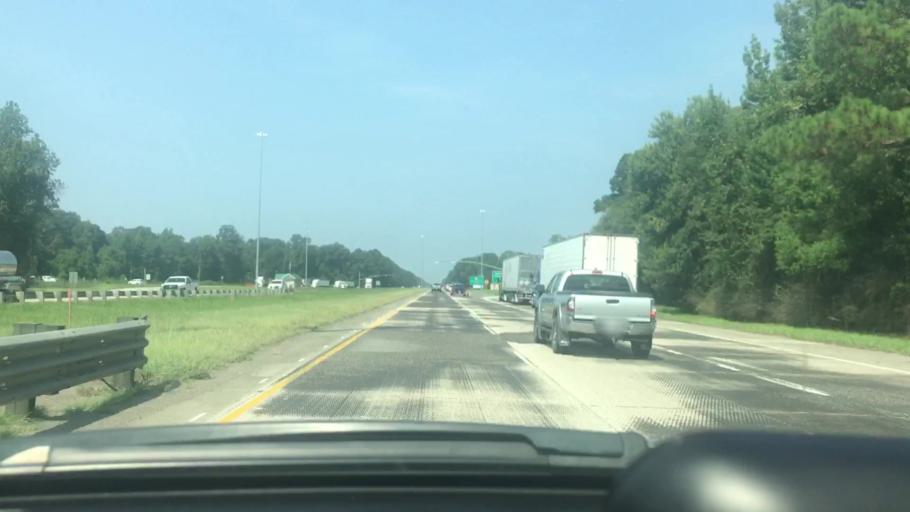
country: US
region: Louisiana
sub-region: Tangipahoa Parish
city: Hammond
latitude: 30.4796
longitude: -90.5180
